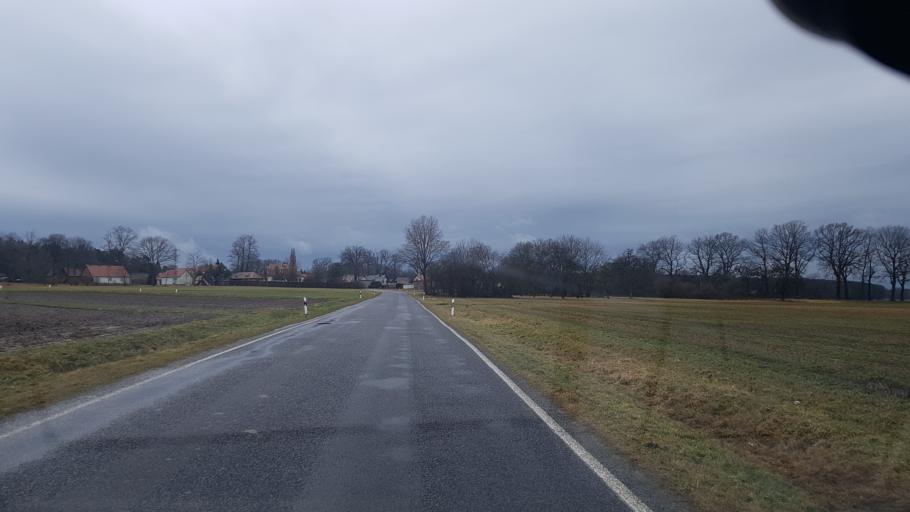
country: DE
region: Brandenburg
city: Neupetershain
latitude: 51.6221
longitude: 14.1091
